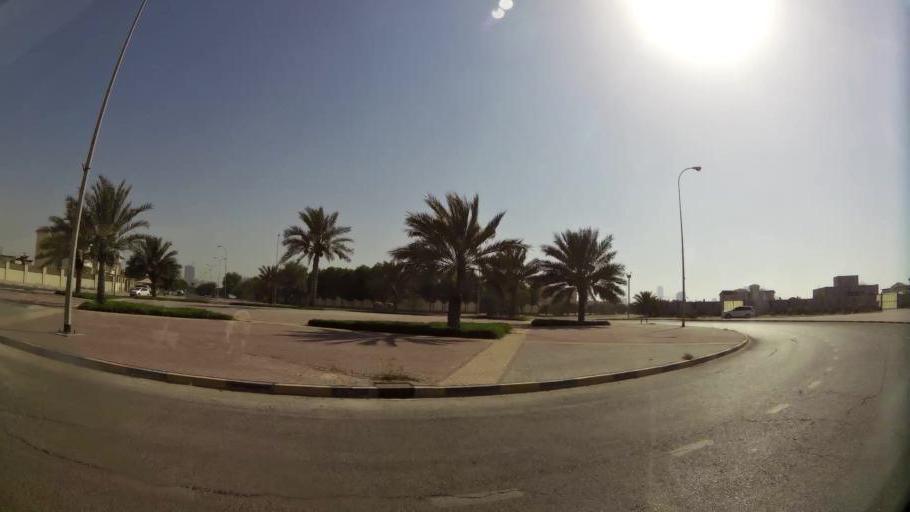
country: AE
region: Ajman
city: Ajman
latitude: 25.4124
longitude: 55.4676
